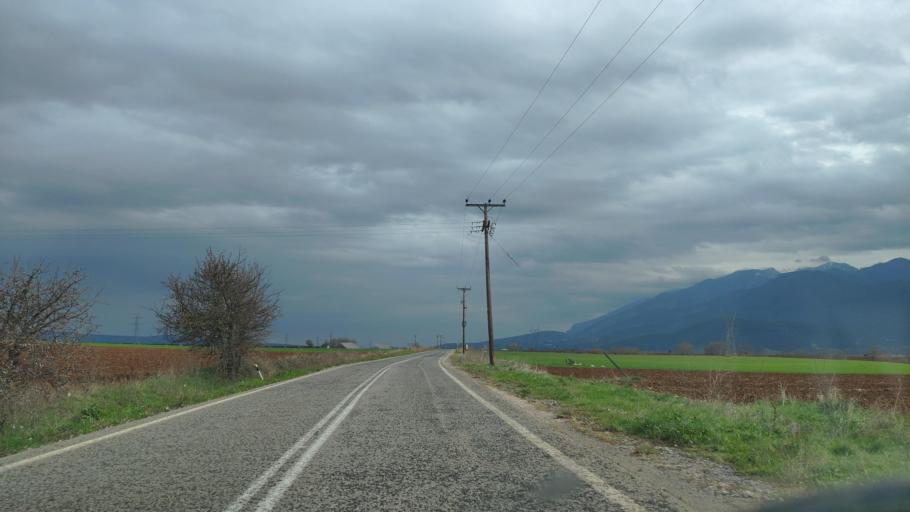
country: GR
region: Central Greece
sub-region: Nomos Fthiotidos
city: Amfikleia
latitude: 38.6990
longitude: 22.5176
